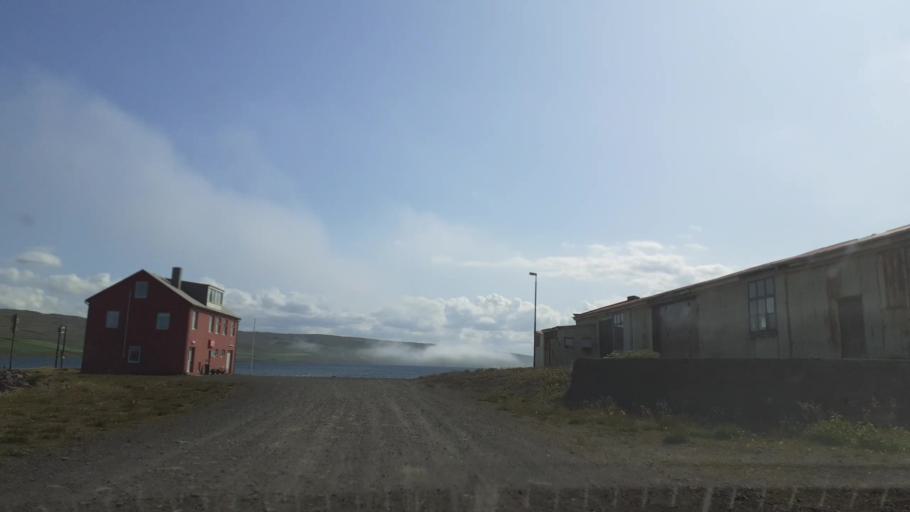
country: IS
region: West
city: Borgarnes
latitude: 65.2098
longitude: -21.0950
